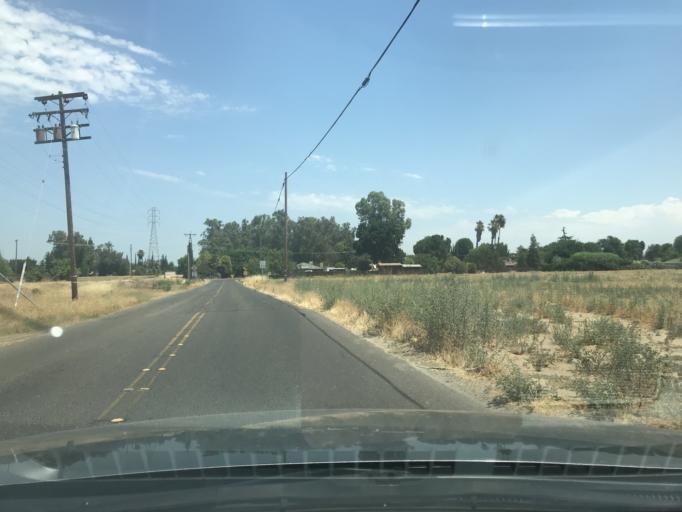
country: US
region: California
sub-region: Merced County
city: Atwater
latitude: 37.3626
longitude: -120.6129
